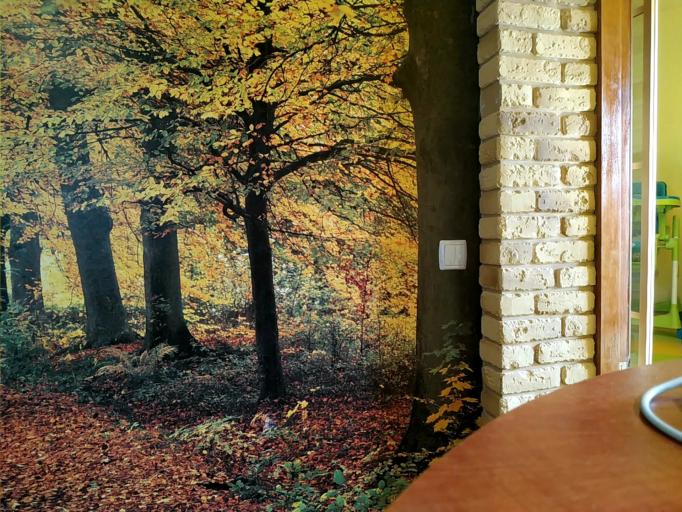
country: RU
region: Tverskaya
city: Kalashnikovo
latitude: 57.3361
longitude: 35.3145
